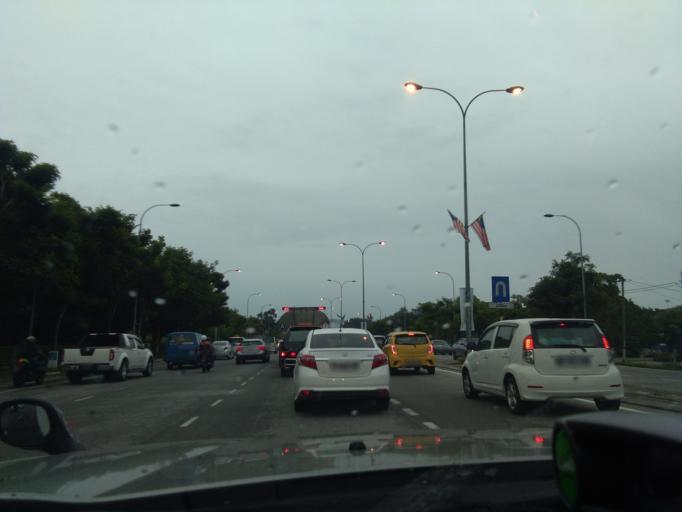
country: MY
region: Penang
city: Nibong Tebal
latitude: 5.1853
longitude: 100.4866
